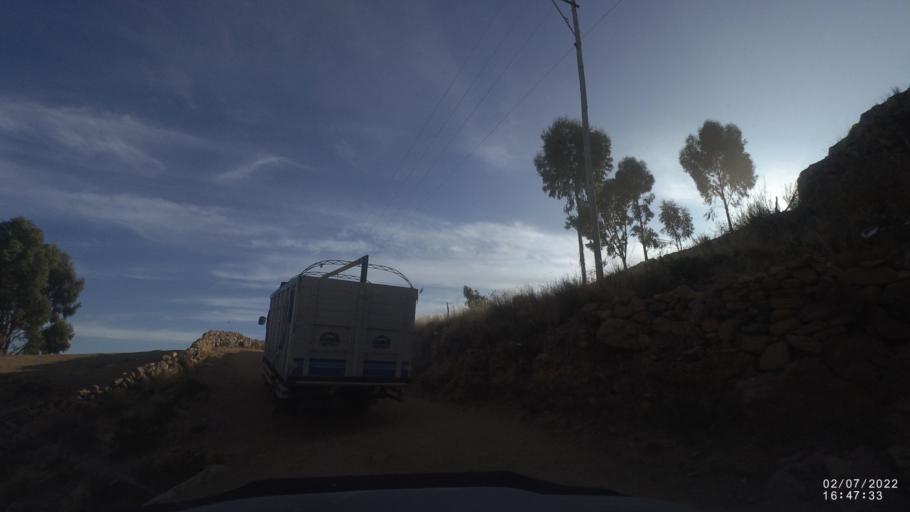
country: BO
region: Cochabamba
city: Irpa Irpa
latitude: -17.9785
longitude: -66.5150
